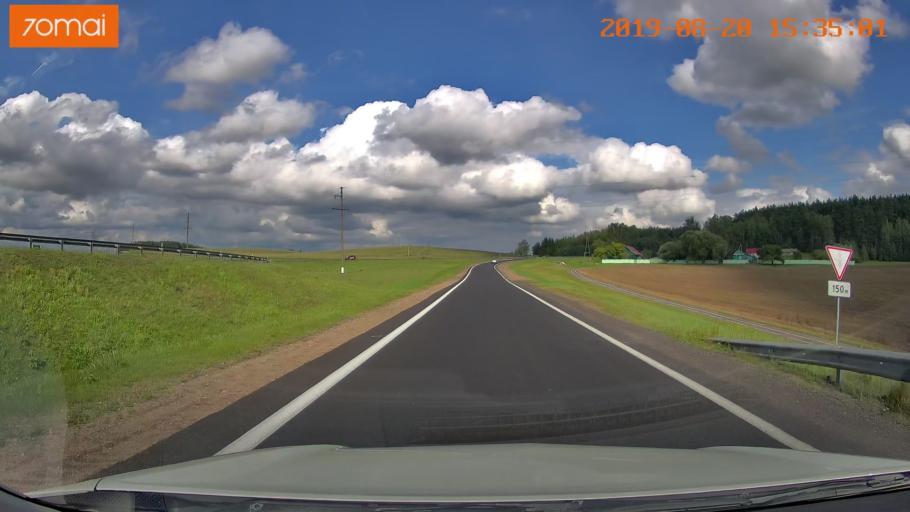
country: BY
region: Minsk
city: Astrashytski Haradok
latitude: 54.0532
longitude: 27.7062
